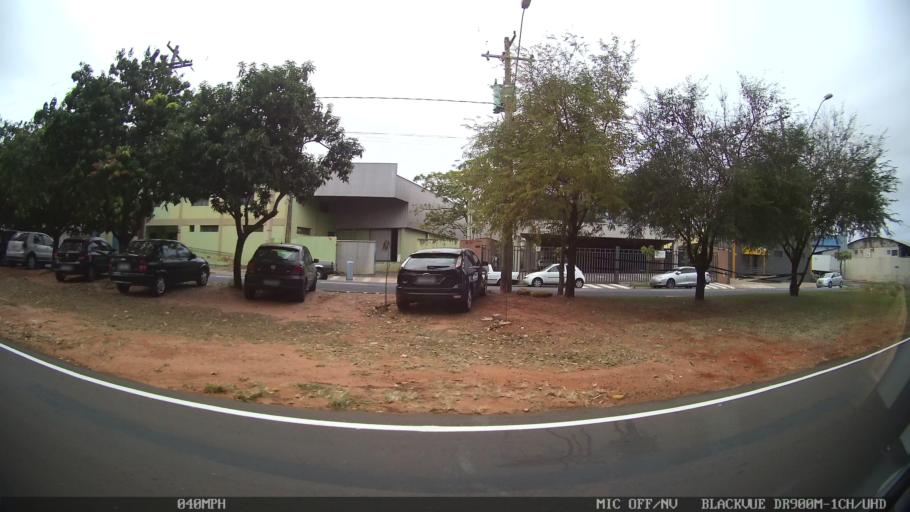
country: BR
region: Sao Paulo
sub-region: Sao Jose Do Rio Preto
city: Sao Jose do Rio Preto
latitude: -20.8290
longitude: -49.4253
